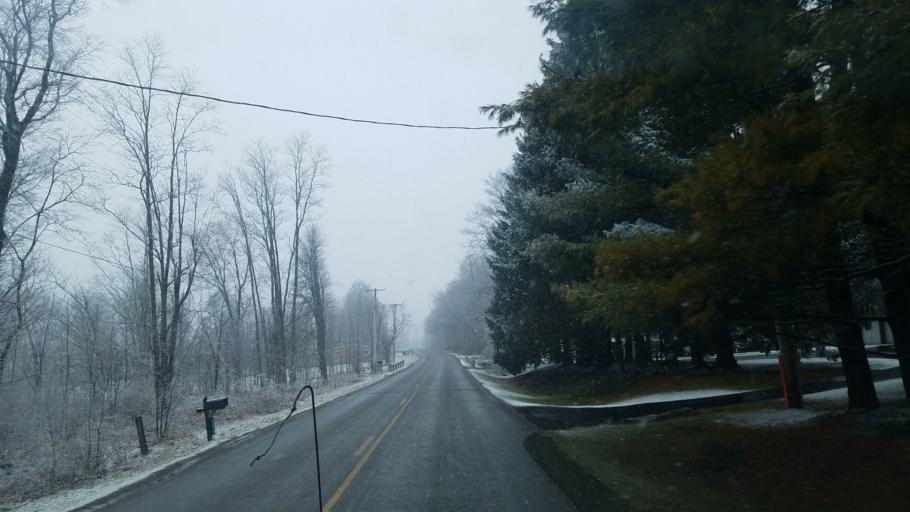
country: US
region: Ohio
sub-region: Logan County
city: Bellefontaine
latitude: 40.3315
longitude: -83.6697
